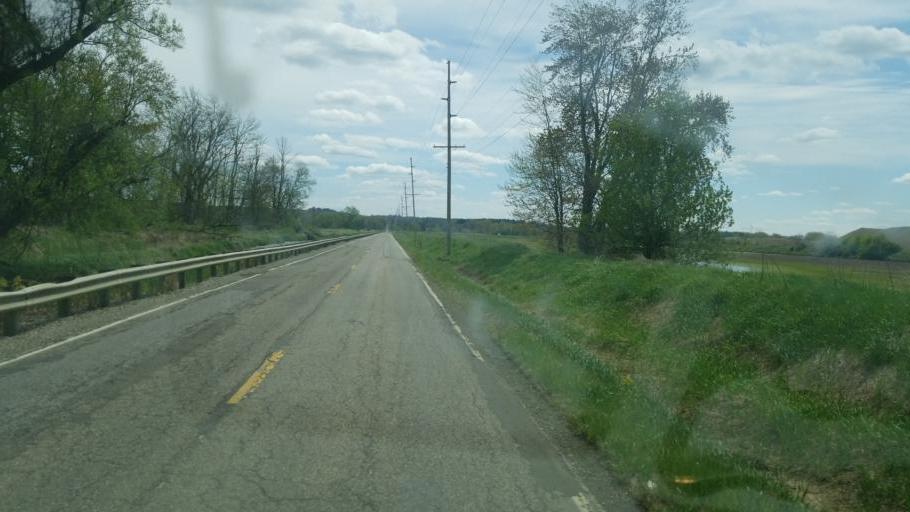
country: US
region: Ohio
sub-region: Wayne County
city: Wooster
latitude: 40.7546
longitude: -81.9443
